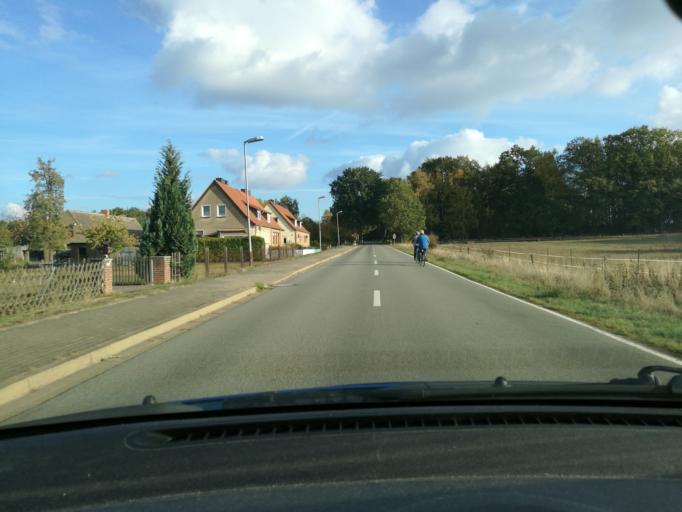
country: DE
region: Saxony-Anhalt
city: Luftkurort Arendsee
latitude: 52.8902
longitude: 11.4444
